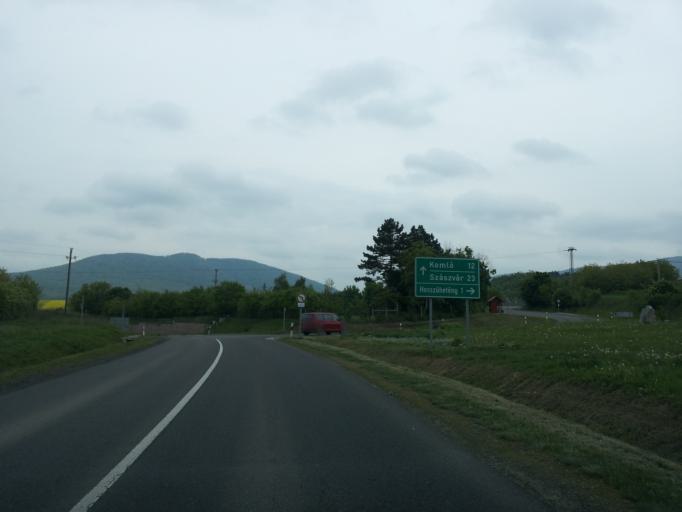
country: HU
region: Baranya
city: Hosszuheteny
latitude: 46.1440
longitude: 18.3490
